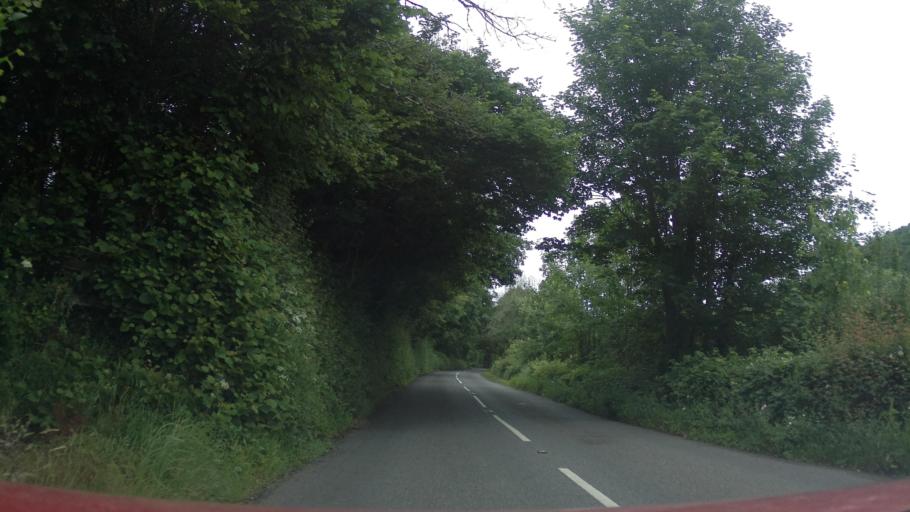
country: GB
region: England
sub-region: Devon
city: Chudleigh
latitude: 50.6608
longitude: -3.6430
